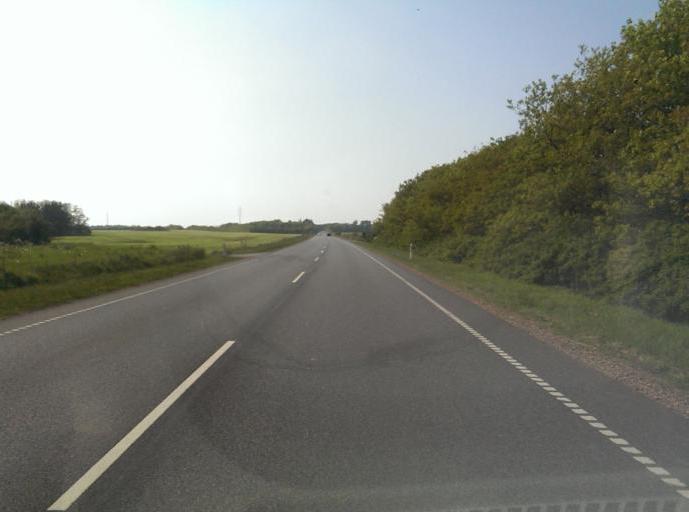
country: DK
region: South Denmark
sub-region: Esbjerg Kommune
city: Tjaereborg
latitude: 55.4998
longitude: 8.6134
